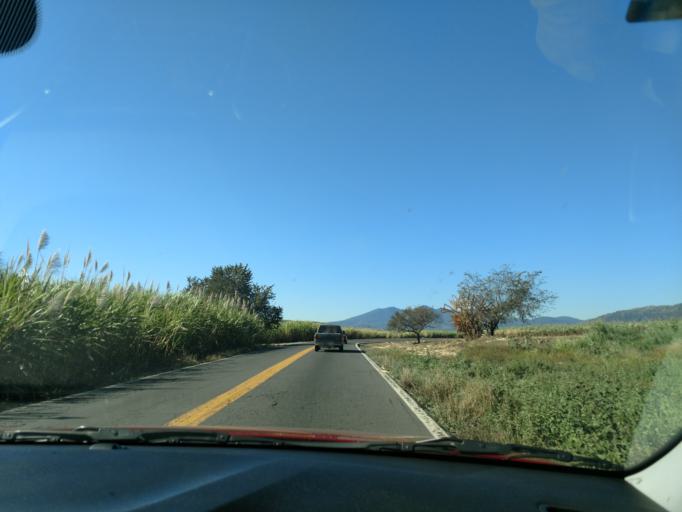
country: MX
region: Nayarit
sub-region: Ahuacatlan
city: Ahuacatlan
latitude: 21.1323
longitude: -104.6051
